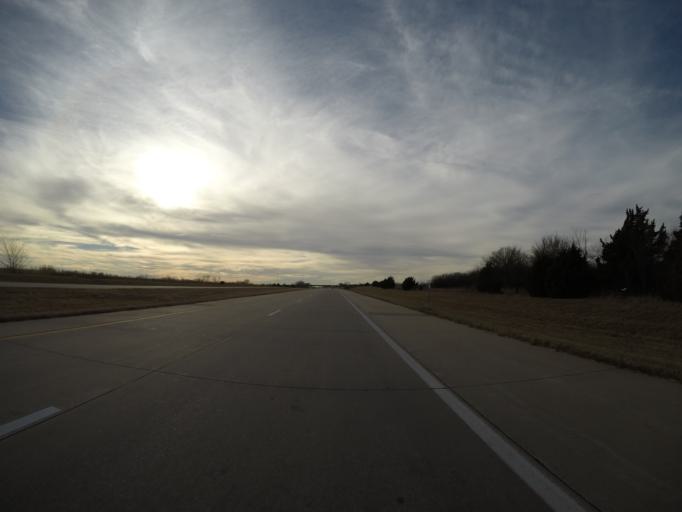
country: US
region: Kansas
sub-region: Franklin County
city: Ottawa
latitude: 38.5303
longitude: -95.3909
